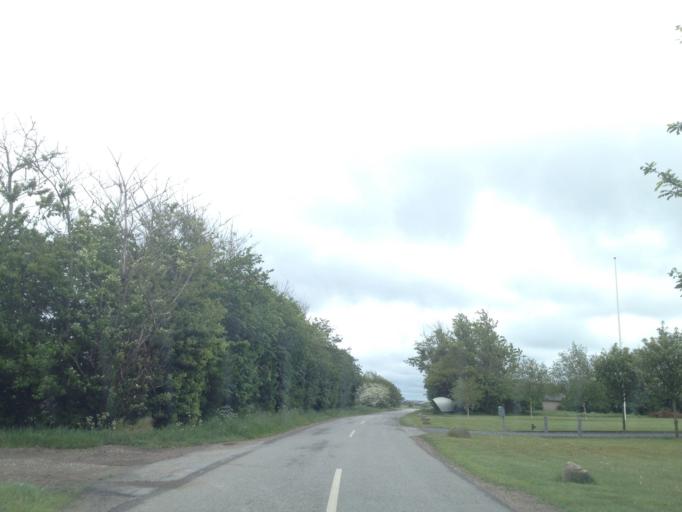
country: DK
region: South Denmark
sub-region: Tonder Kommune
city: Sherrebek
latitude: 55.0987
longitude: 8.7426
